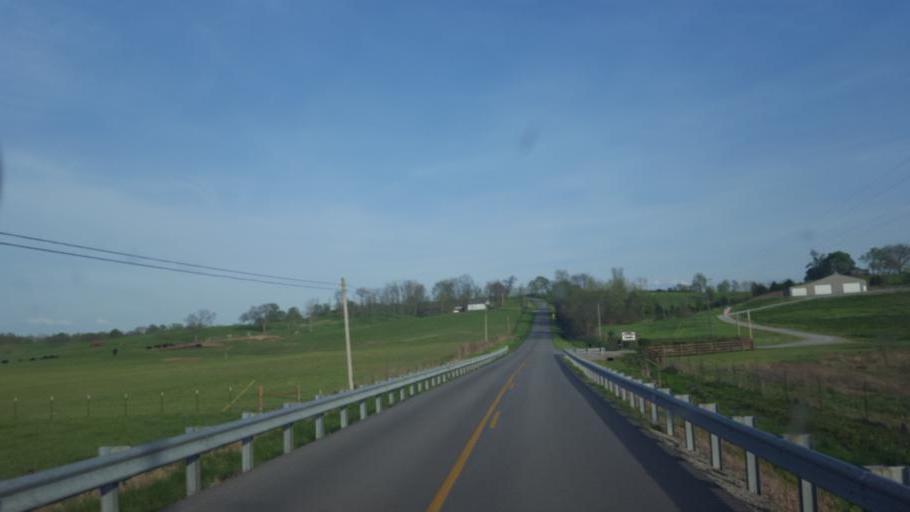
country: US
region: Kentucky
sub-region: Allen County
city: Scottsville
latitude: 36.8886
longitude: -86.1446
